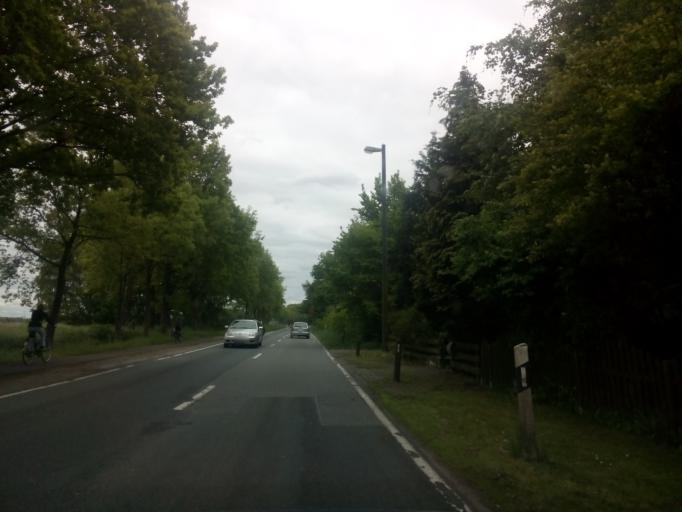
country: DE
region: Lower Saxony
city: Stuhr
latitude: 53.0825
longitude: 8.7035
